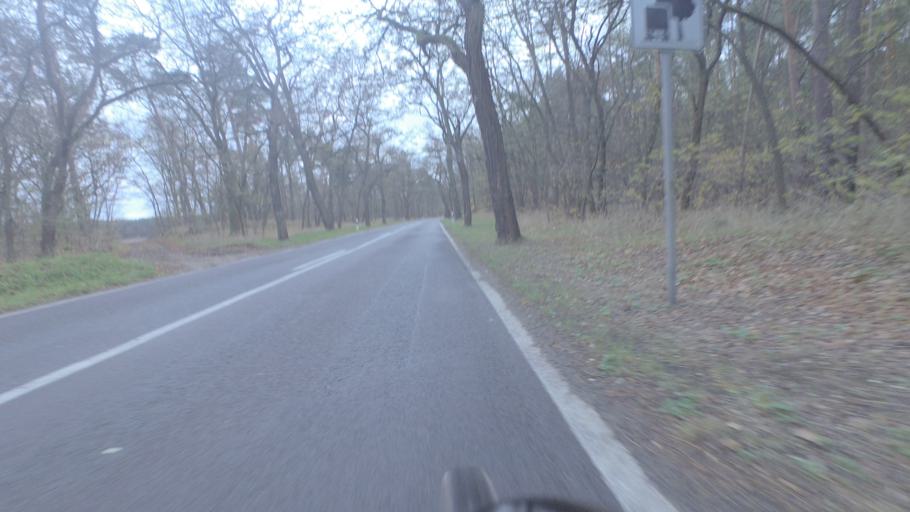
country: DE
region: Brandenburg
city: Michendorf
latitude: 52.3080
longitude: 13.1202
